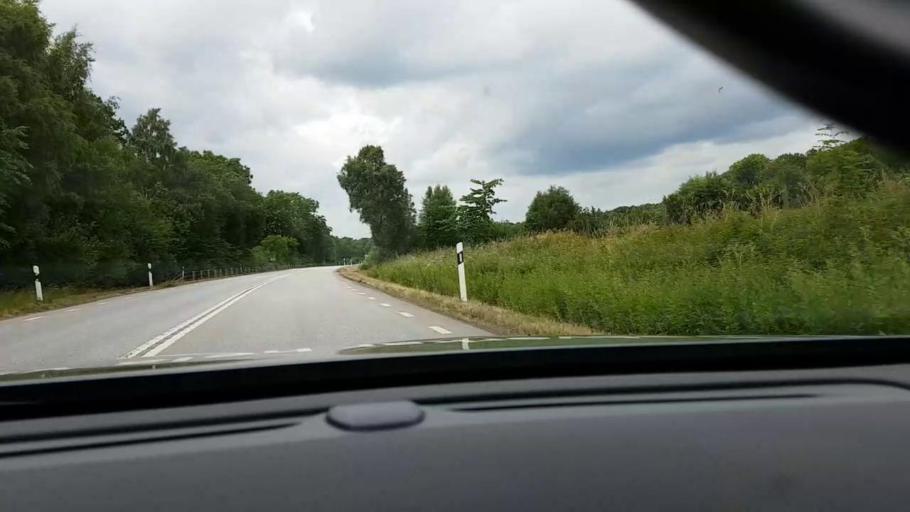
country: SE
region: Skane
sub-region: Horby Kommun
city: Hoerby
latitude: 55.8752
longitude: 13.6321
